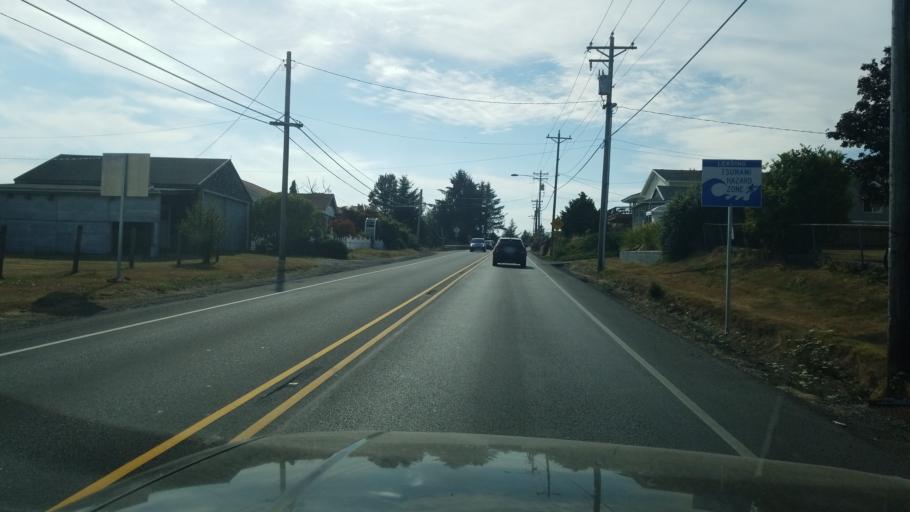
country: US
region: Oregon
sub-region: Tillamook County
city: Bay City
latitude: 45.5582
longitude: -123.9203
